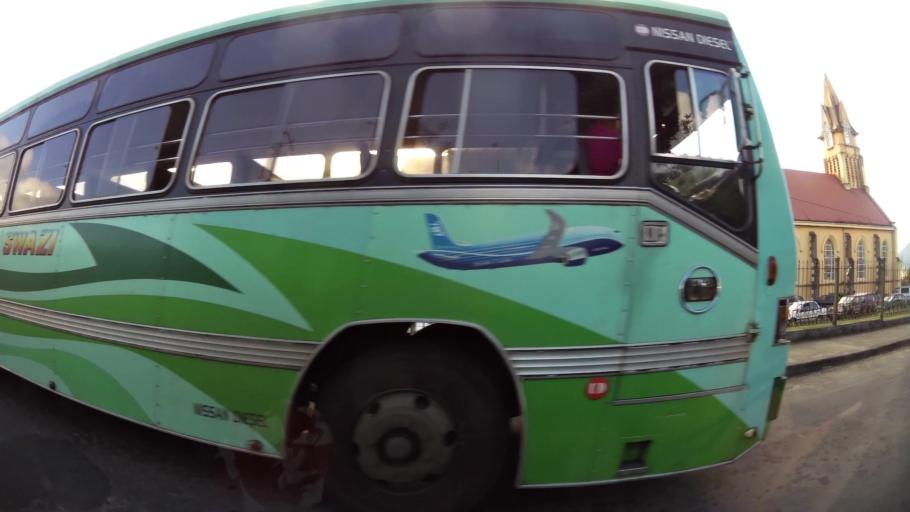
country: MU
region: Plaines Wilhems
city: Quatre Bornes
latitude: -20.2564
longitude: 57.4869
